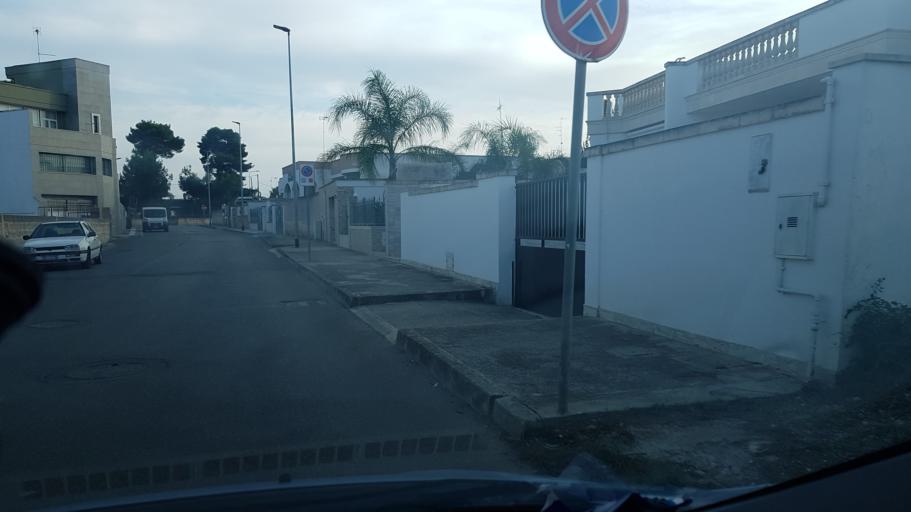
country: IT
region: Apulia
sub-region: Provincia di Lecce
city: Carmiano
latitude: 40.3420
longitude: 18.0397
